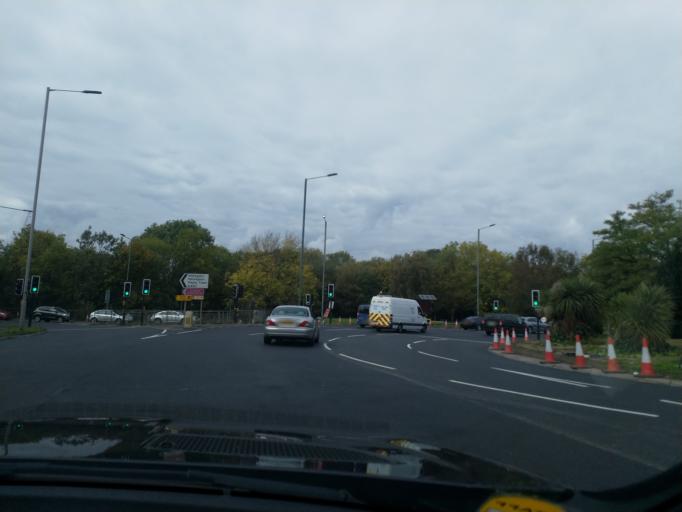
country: GB
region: England
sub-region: Greater London
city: Hayes
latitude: 51.4978
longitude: -0.4097
